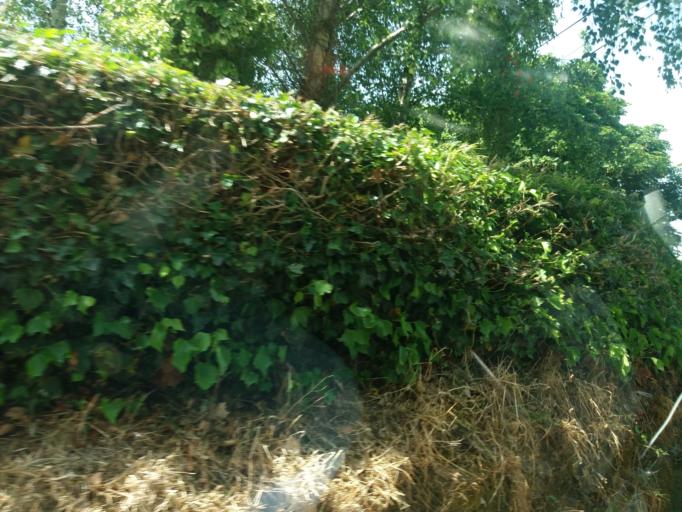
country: IE
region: Leinster
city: Lusk
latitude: 53.5352
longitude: -6.1553
